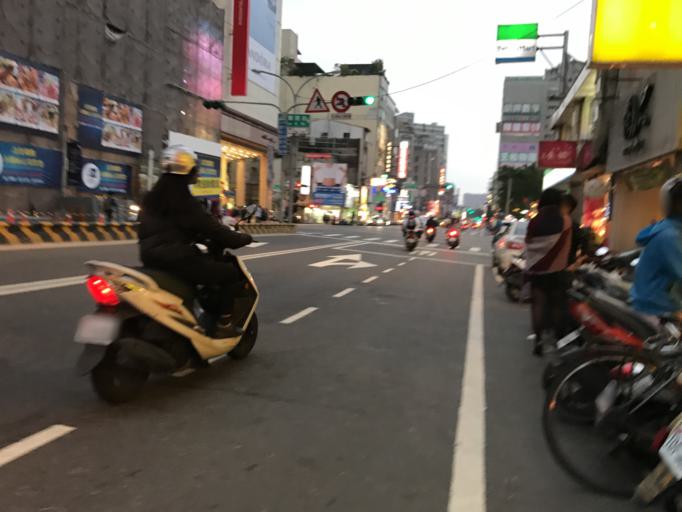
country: TW
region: Taiwan
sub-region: Tainan
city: Tainan
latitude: 22.9959
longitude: 120.2102
